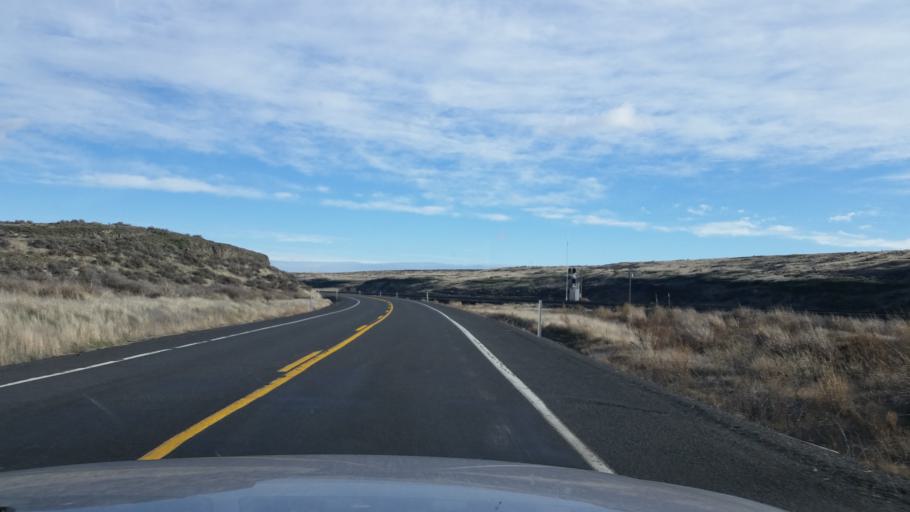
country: US
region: Washington
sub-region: Adams County
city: Ritzville
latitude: 47.3574
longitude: -118.5029
